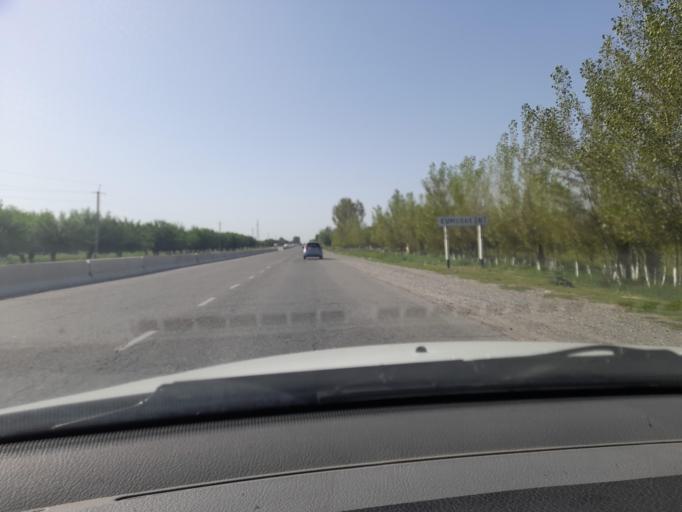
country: UZ
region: Samarqand
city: Daxbet
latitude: 39.8068
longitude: 66.8595
